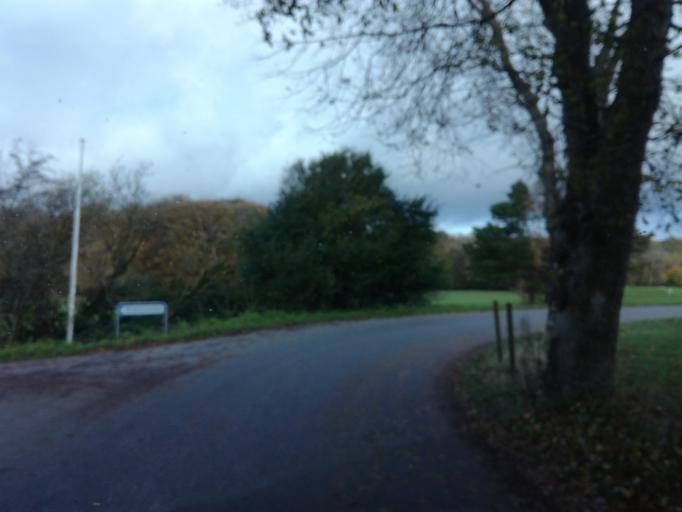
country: DK
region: South Denmark
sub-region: Vejle Kommune
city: Borkop
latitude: 55.6771
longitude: 9.5980
